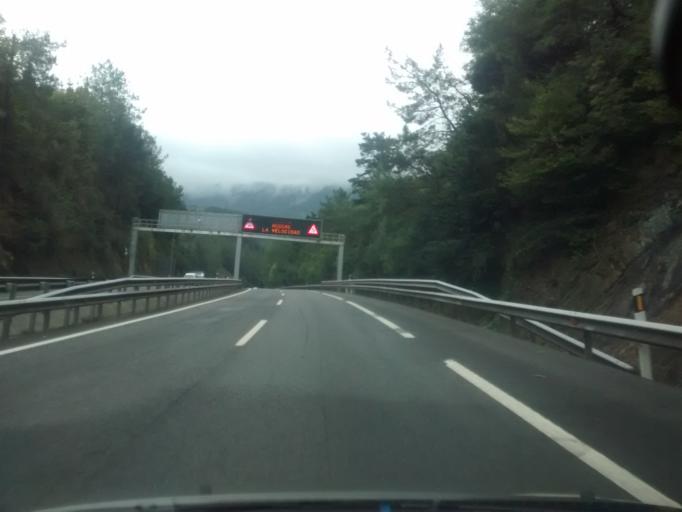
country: ES
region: Basque Country
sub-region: Provincia de Guipuzcoa
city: Elgoibar
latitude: 43.2257
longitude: -2.4032
